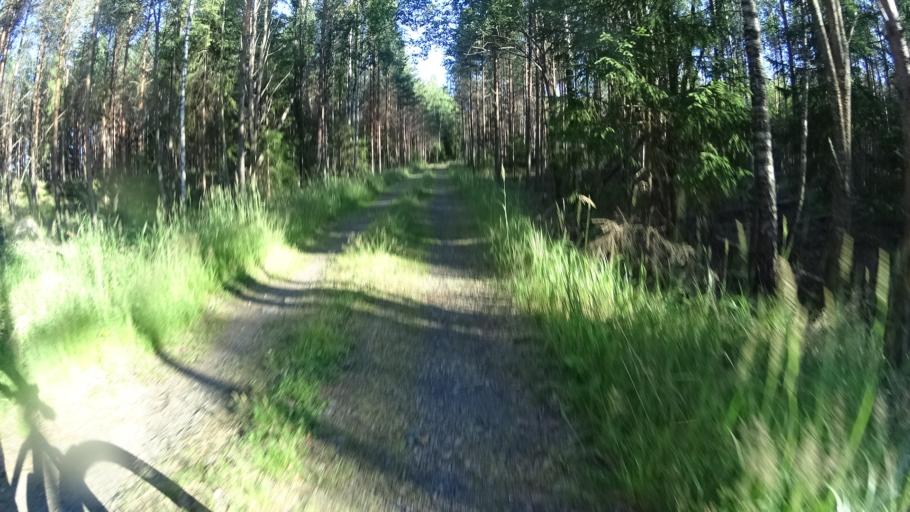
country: FI
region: Uusimaa
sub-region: Helsinki
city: Karkkila
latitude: 60.6641
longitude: 24.1322
